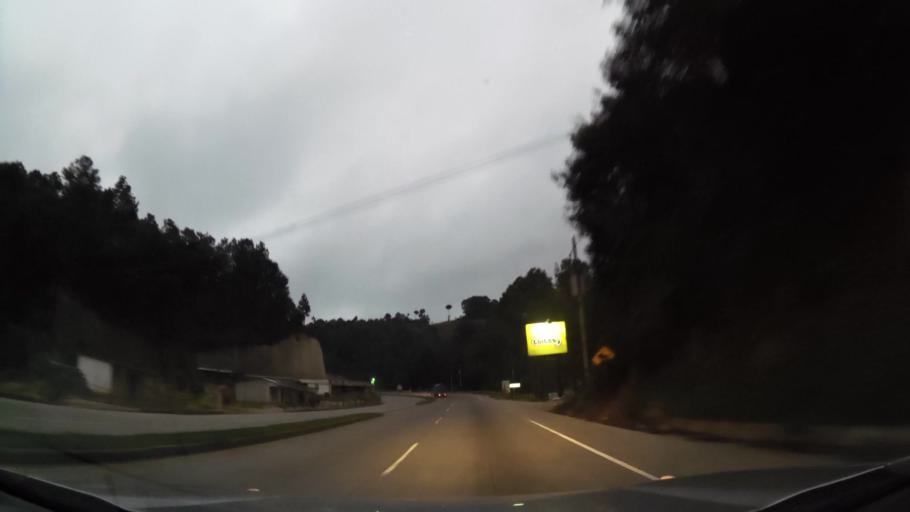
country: GT
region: Chimaltenango
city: Tecpan Guatemala
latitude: 14.8222
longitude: -91.0281
